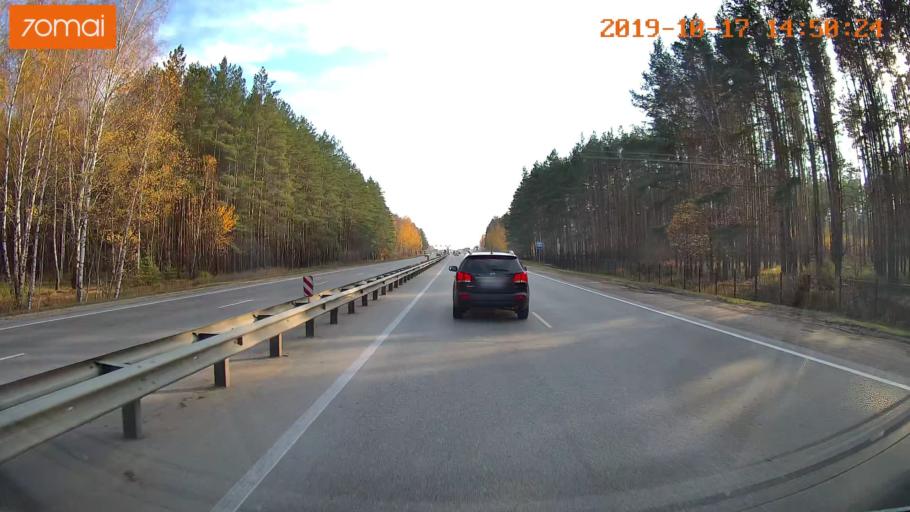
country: RU
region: Rjazan
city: Polyany
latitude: 54.7344
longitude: 39.8421
